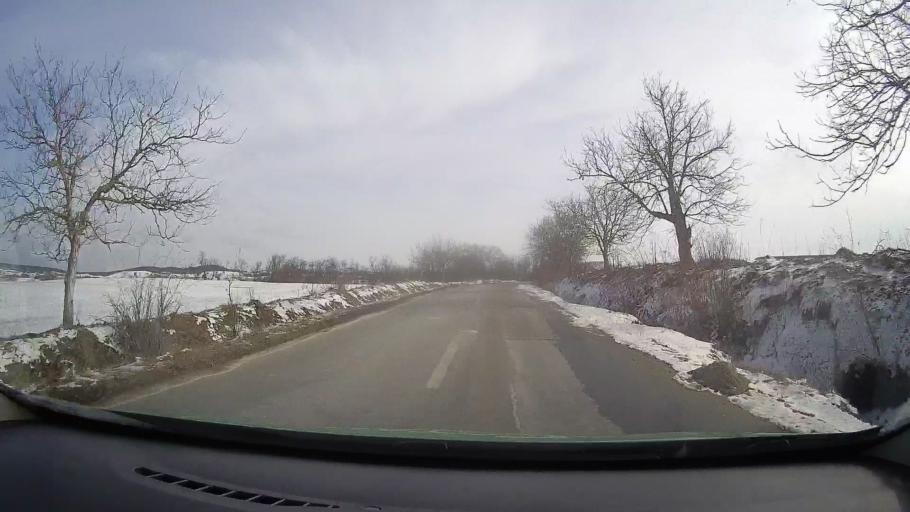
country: RO
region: Mures
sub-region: Comuna Apold
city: Apold
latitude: 46.1152
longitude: 24.8268
